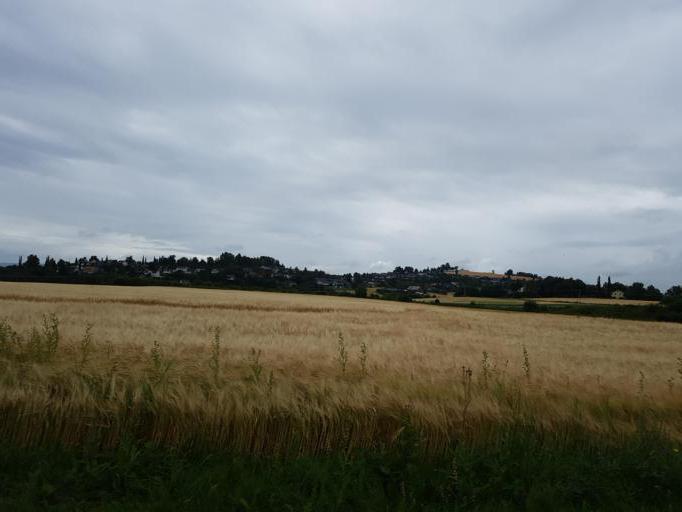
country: NO
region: Nord-Trondelag
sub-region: Levanger
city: Levanger
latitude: 63.7347
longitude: 11.2870
